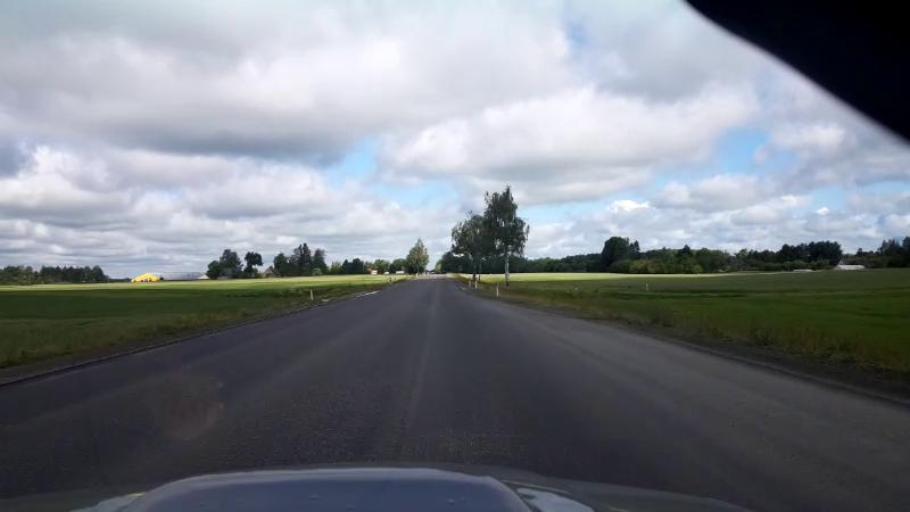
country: LV
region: Bauskas Rajons
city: Bauska
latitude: 56.3171
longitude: 24.3254
